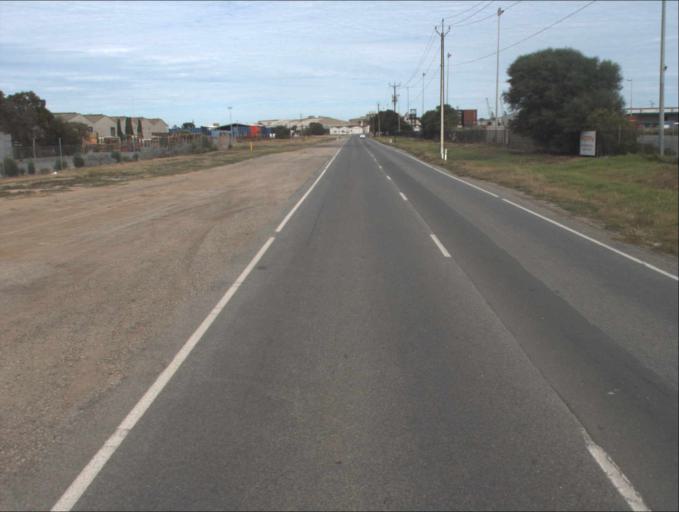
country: AU
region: South Australia
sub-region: Port Adelaide Enfield
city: Birkenhead
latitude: -34.8291
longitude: 138.5185
